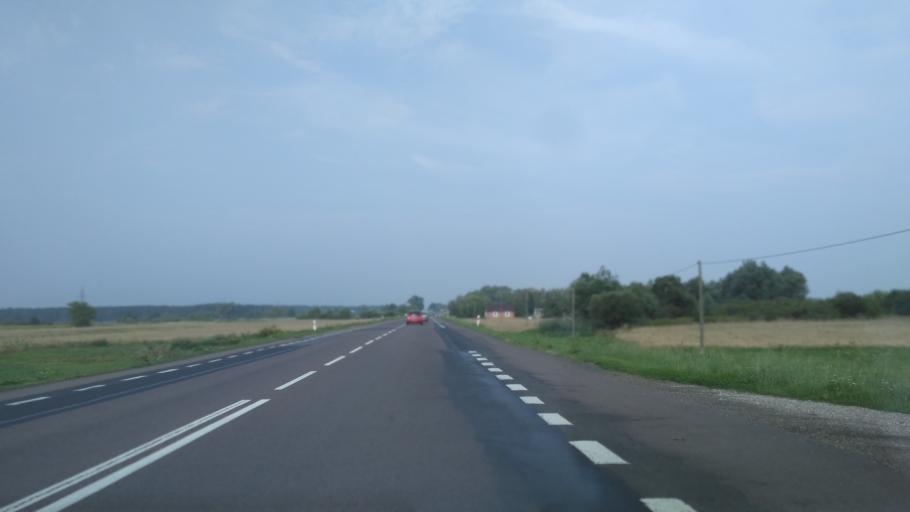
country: PL
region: Lublin Voivodeship
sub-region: Powiat swidnicki
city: Trawniki
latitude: 51.1623
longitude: 23.0049
